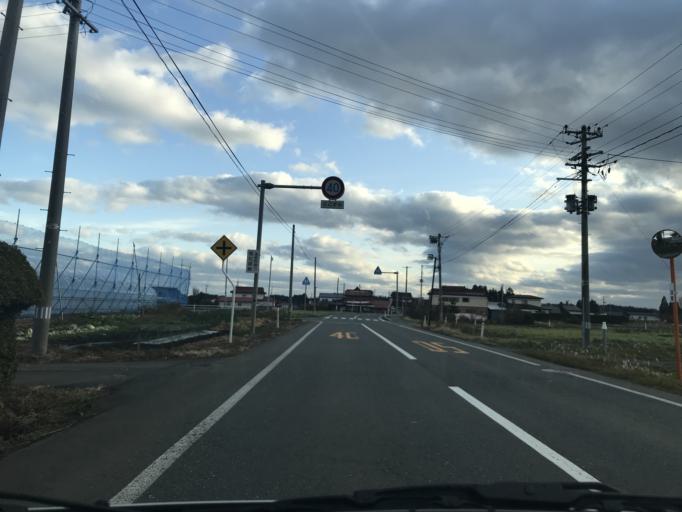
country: JP
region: Iwate
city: Mizusawa
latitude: 39.1320
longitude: 141.0529
